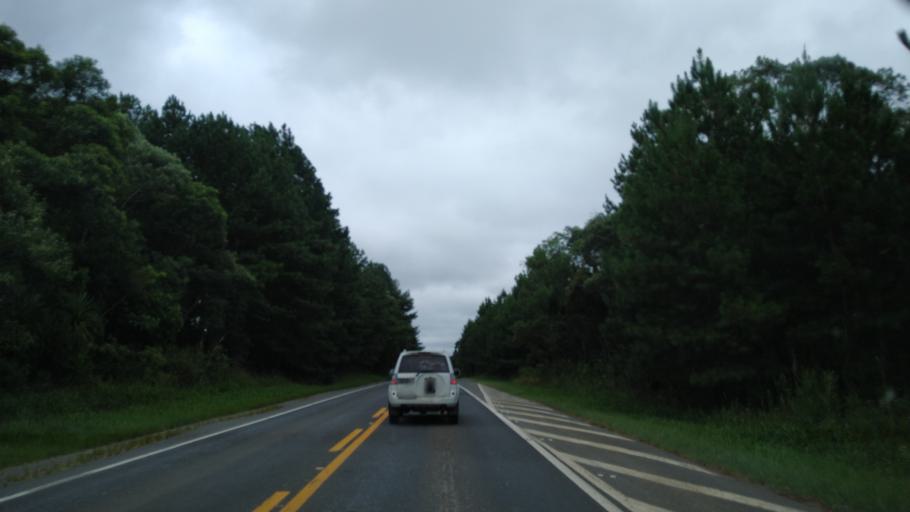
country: BR
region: Santa Catarina
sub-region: Tres Barras
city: Tres Barras
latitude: -26.1806
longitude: -50.1958
